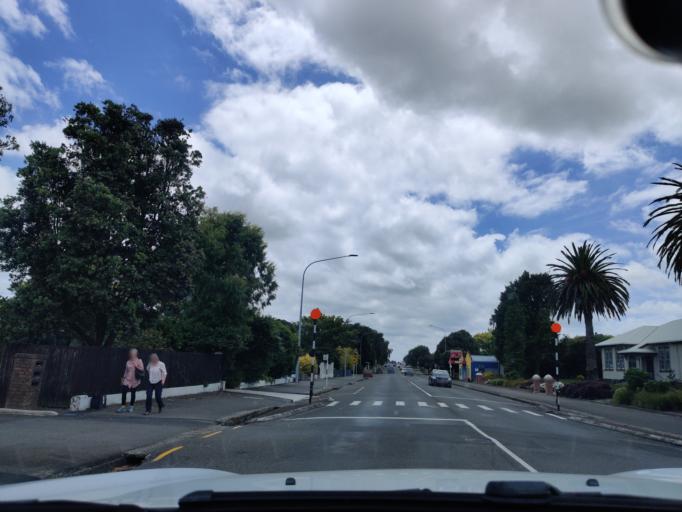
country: NZ
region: Manawatu-Wanganui
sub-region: Palmerston North City
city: Palmerston North
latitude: -40.3574
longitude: 175.6296
